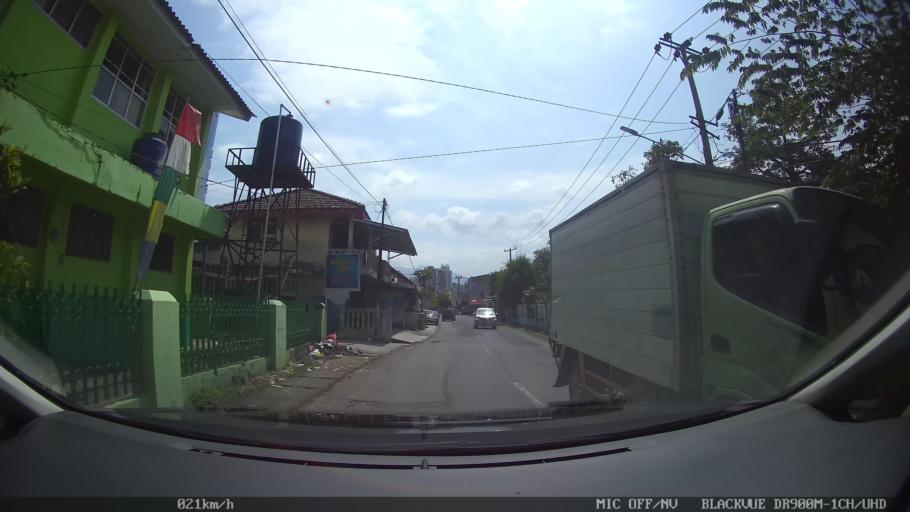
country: ID
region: Lampung
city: Bandarlampung
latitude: -5.4144
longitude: 105.2607
